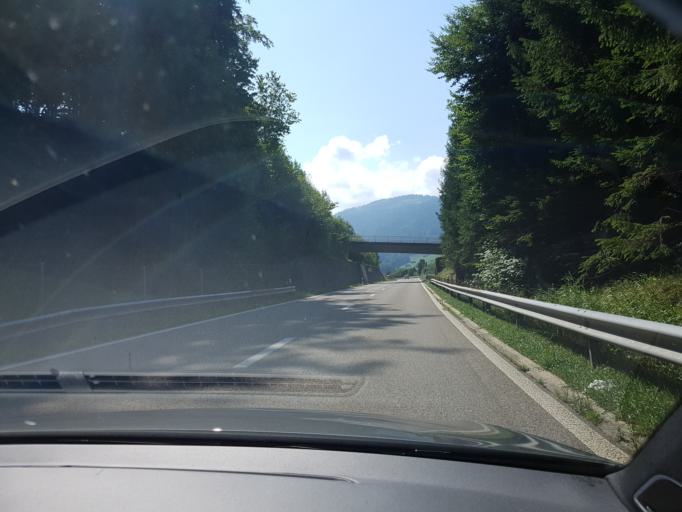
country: CH
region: Saint Gallen
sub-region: Wahlkreis Toggenburg
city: Ebnat-Kappel
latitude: 47.2636
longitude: 9.1320
